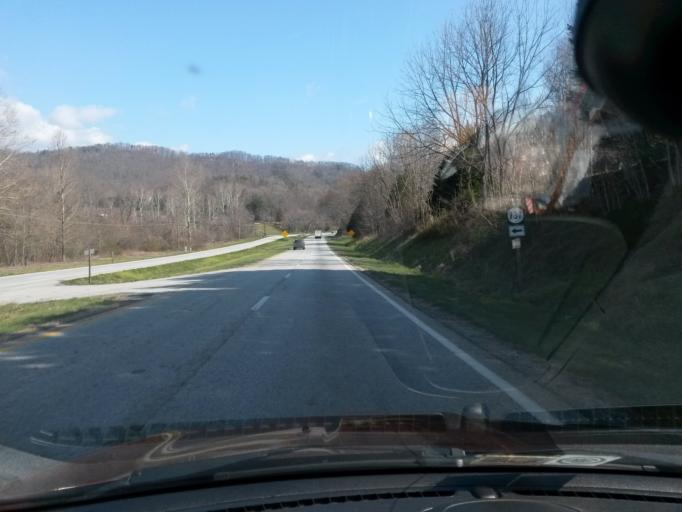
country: US
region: Virginia
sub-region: Nelson County
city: Lovingston
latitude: 37.8018
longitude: -78.8620
